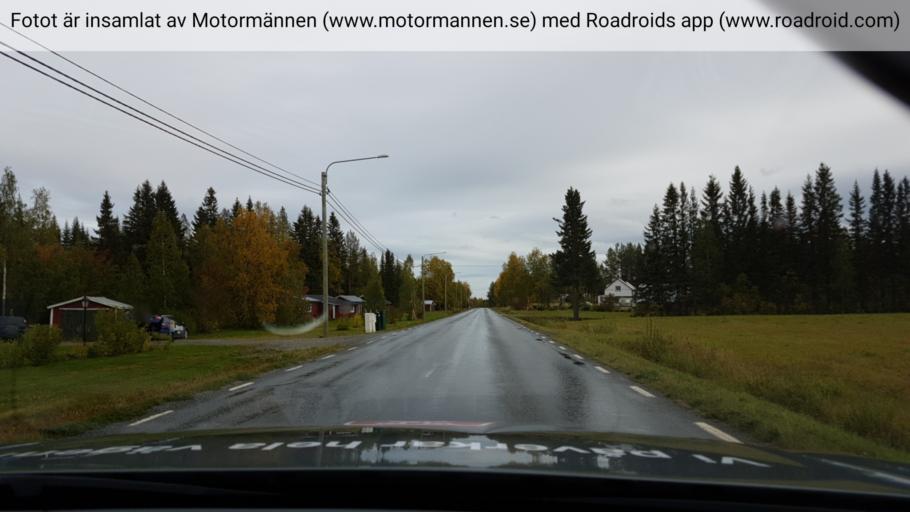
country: SE
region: Vaesterbotten
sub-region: Vilhelmina Kommun
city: Sjoberg
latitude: 64.6505
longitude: 16.3331
